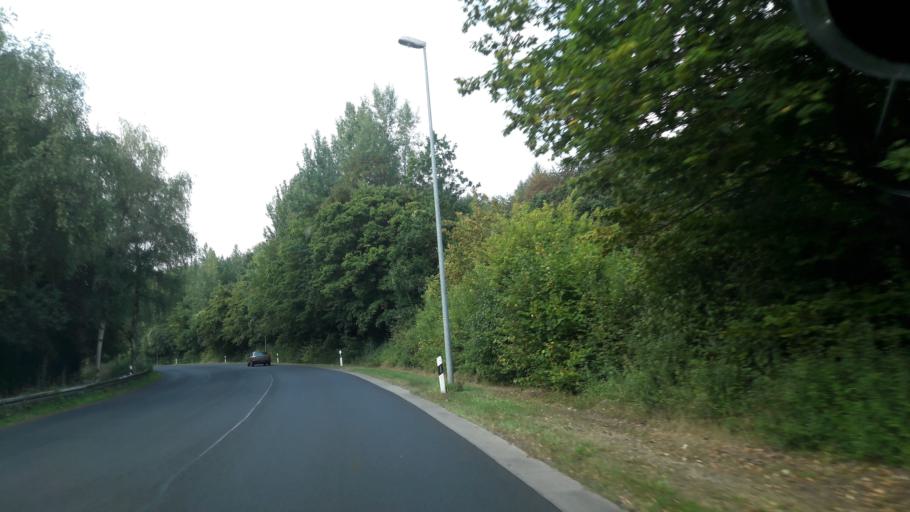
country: DE
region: Lower Saxony
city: Diekholzen
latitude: 52.1249
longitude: 9.9044
